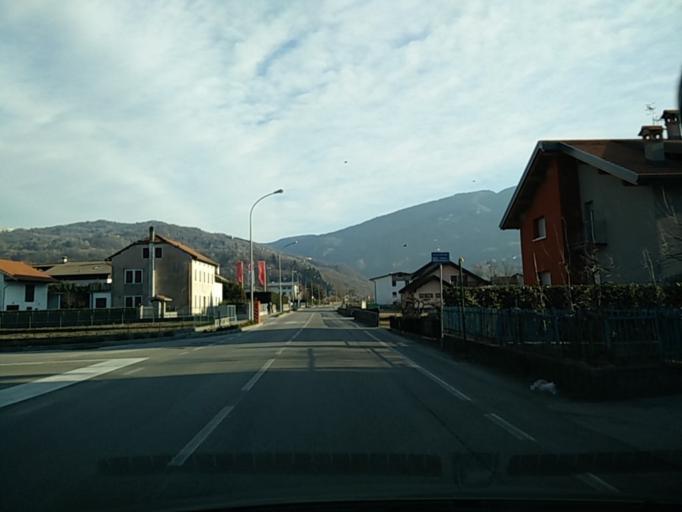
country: IT
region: Veneto
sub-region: Provincia di Belluno
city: Farra d'Alpago
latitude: 46.1304
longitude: 12.3457
